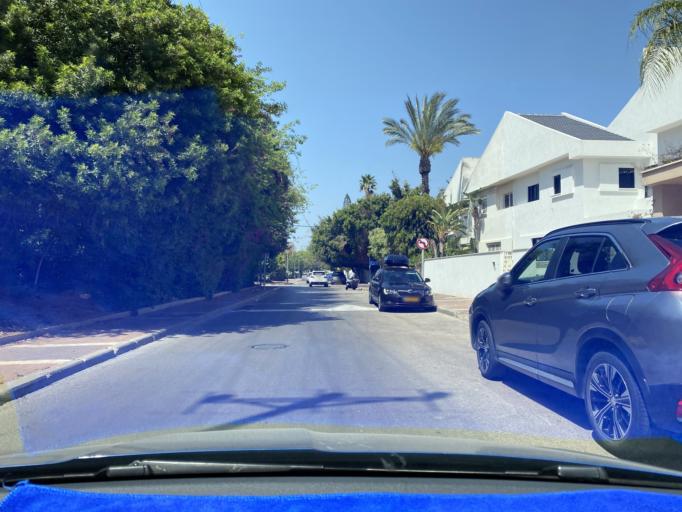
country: IL
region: Tel Aviv
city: Kefar Shemaryahu
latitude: 32.1767
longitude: 34.8143
